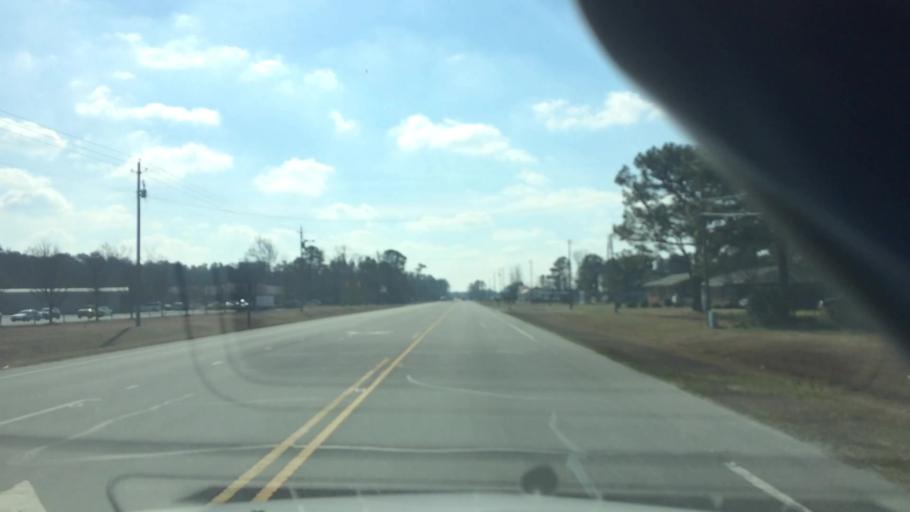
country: US
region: North Carolina
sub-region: Duplin County
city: Beulaville
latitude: 35.0767
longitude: -77.7339
